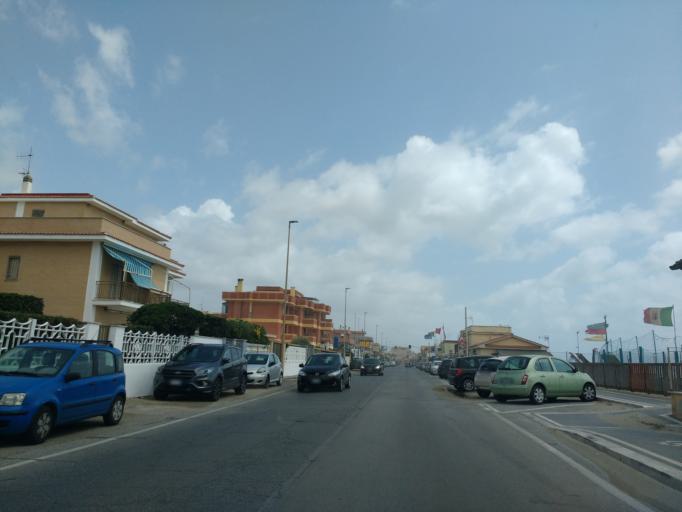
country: IT
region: Latium
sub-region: Citta metropolitana di Roma Capitale
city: Ardea
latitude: 41.5842
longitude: 12.5015
